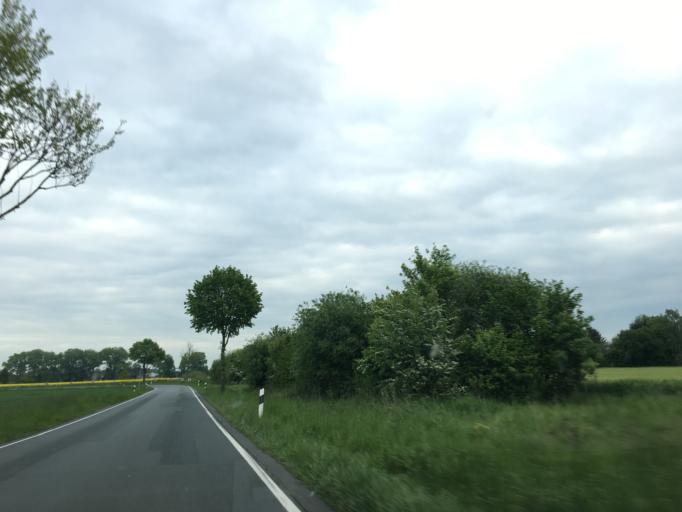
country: DE
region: Lower Saxony
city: Gross Munzel
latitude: 52.3809
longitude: 9.4422
